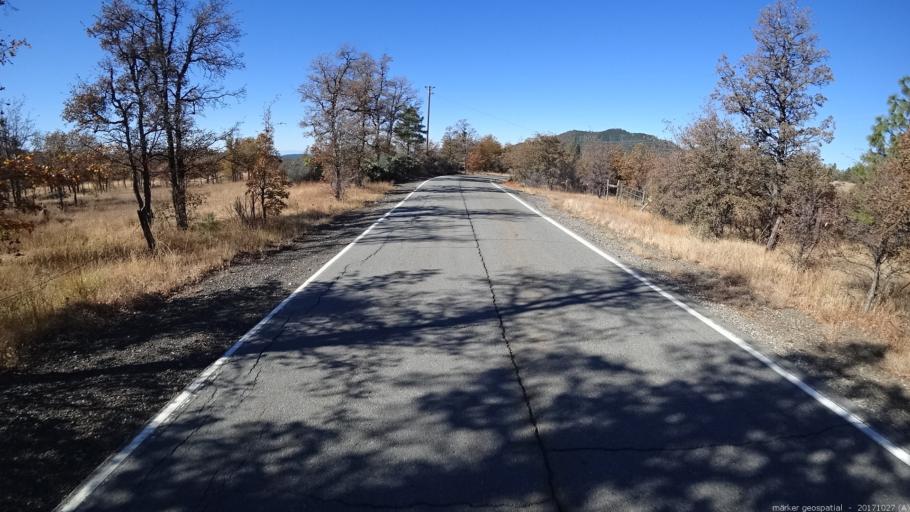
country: US
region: California
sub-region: Shasta County
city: Burney
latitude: 40.7961
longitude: -121.9183
